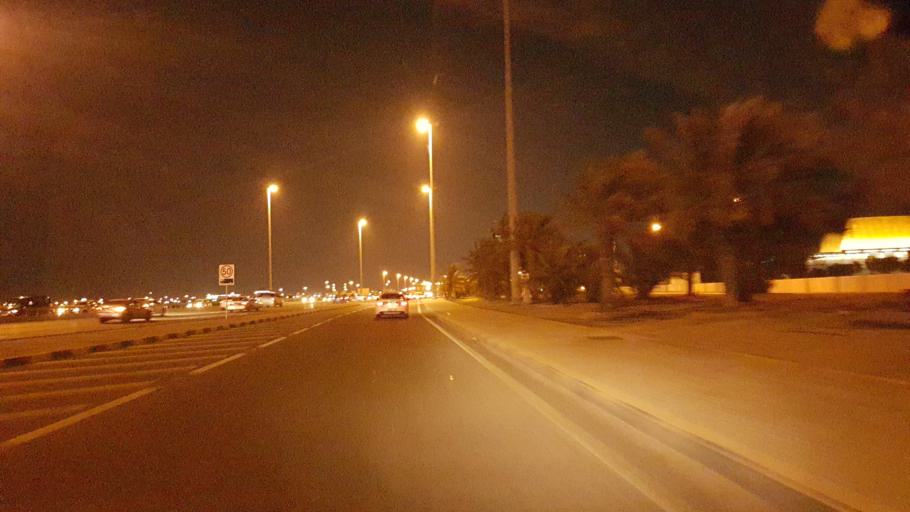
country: BH
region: Muharraq
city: Al Muharraq
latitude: 26.2425
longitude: 50.5955
